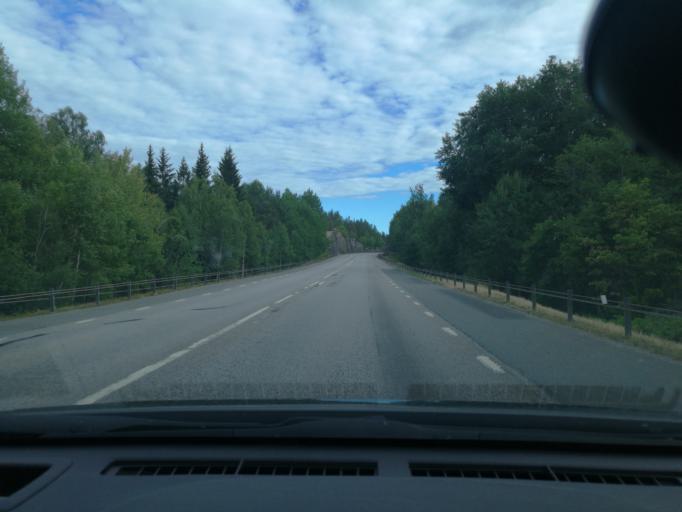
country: SE
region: Kalmar
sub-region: Vasterviks Kommun
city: Ankarsrum
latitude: 57.6503
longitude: 16.4415
